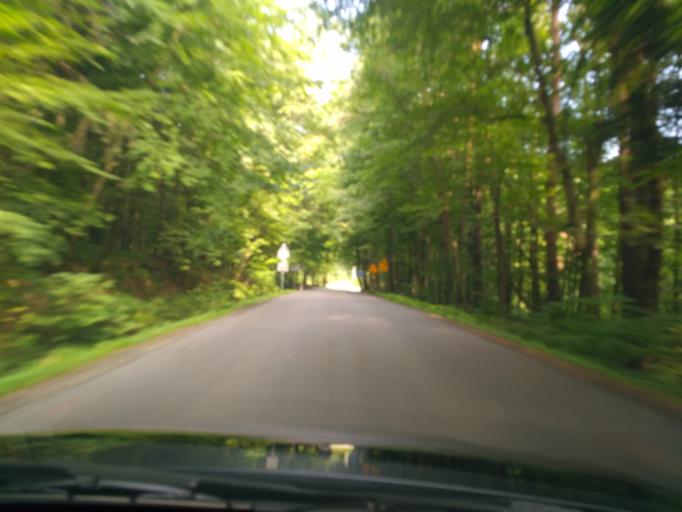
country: PL
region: Subcarpathian Voivodeship
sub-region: Powiat strzyzowski
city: Czudec
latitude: 49.9657
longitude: 21.8409
